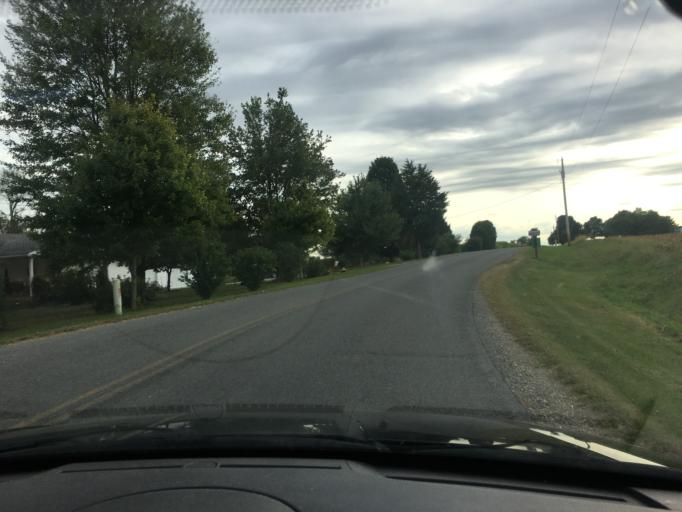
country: US
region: Ohio
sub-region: Logan County
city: West Liberty
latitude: 40.2914
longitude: -83.6845
